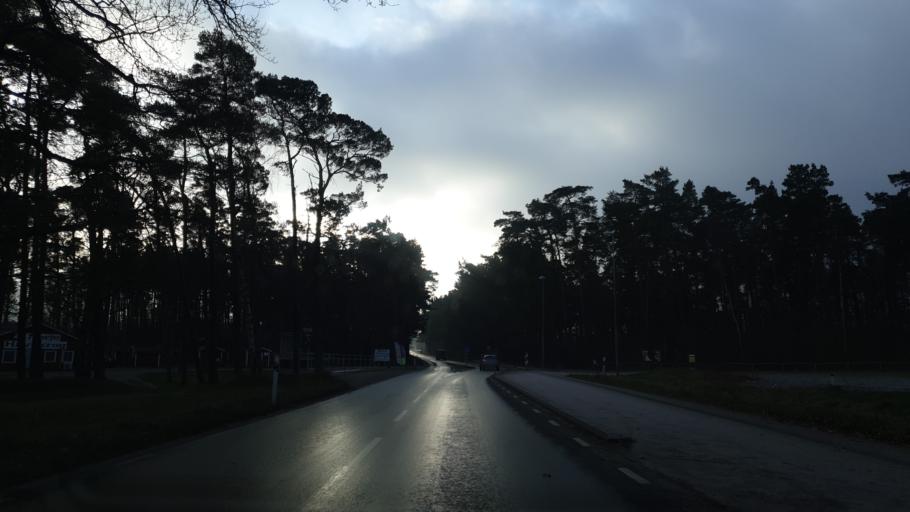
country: SE
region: Blekinge
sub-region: Karlshamns Kommun
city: Morrum
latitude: 56.1265
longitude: 14.6737
